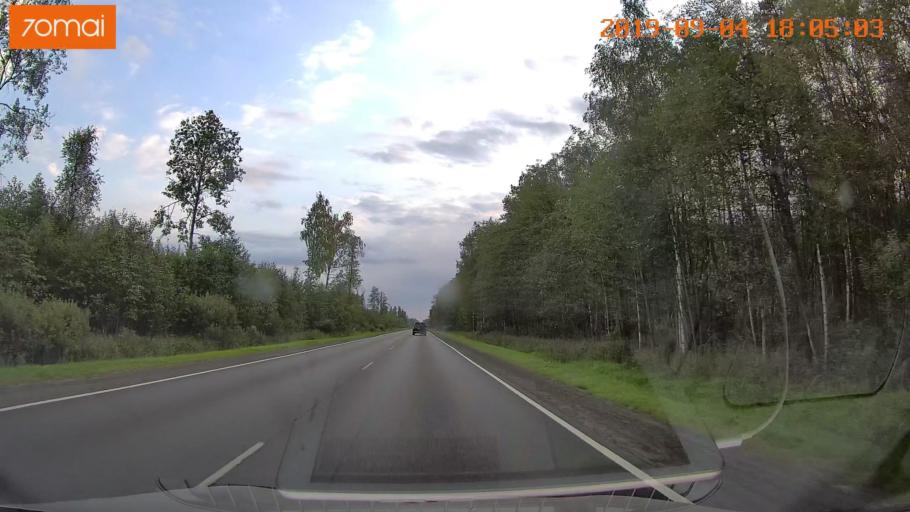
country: RU
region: Moskovskaya
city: Il'inskiy Pogost
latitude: 55.4454
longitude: 38.8312
